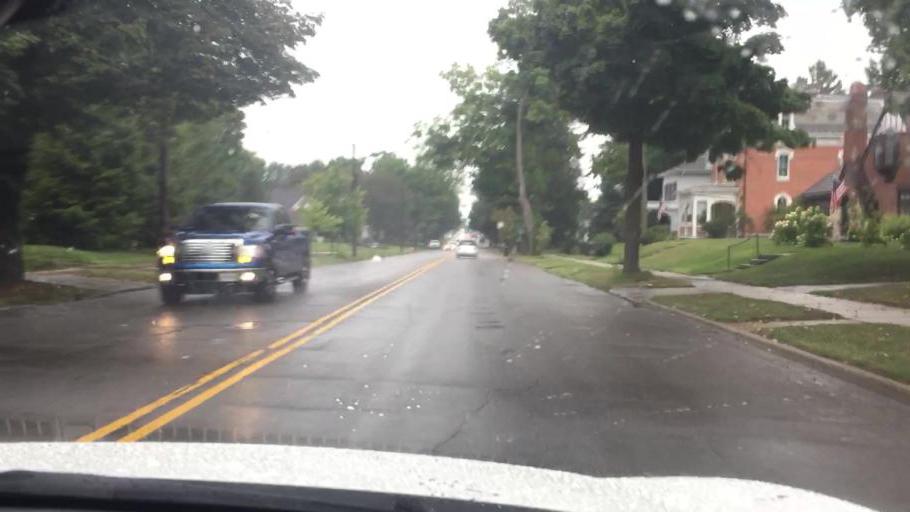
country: US
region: Ohio
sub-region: Champaign County
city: Urbana
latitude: 40.1077
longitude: -83.7453
